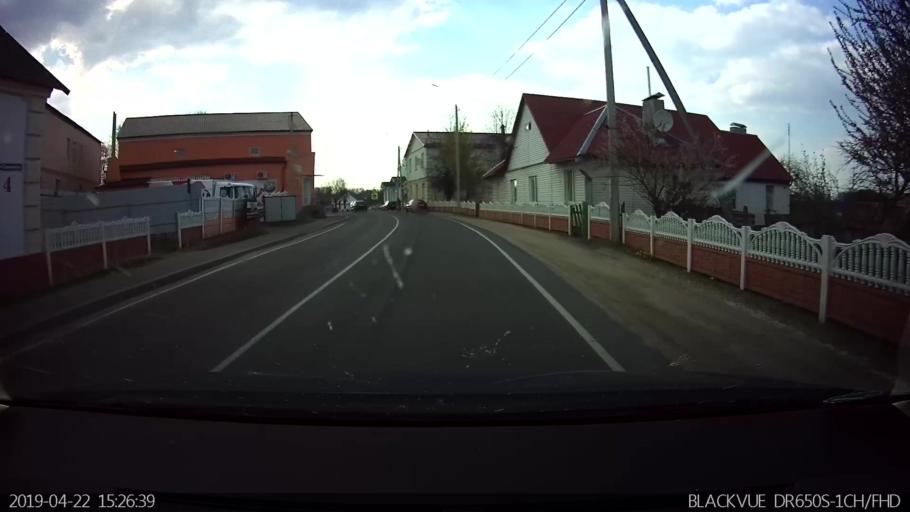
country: BY
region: Brest
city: Vysokaye
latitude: 52.3683
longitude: 23.3779
